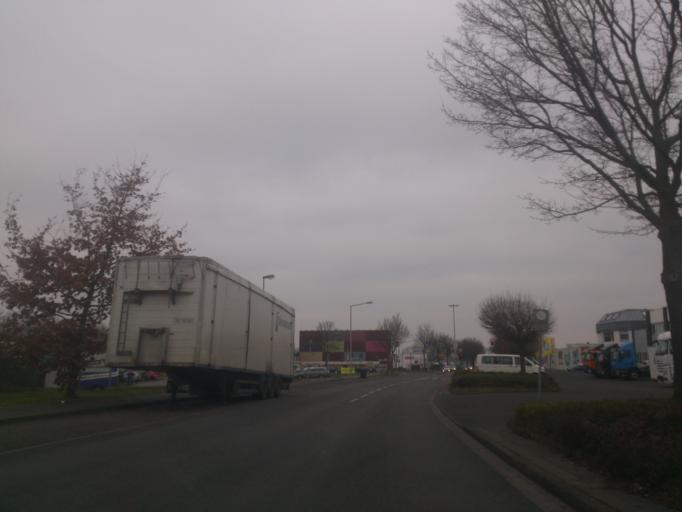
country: DE
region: North Rhine-Westphalia
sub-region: Regierungsbezirk Detmold
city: Paderborn
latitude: 51.7292
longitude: 8.7868
